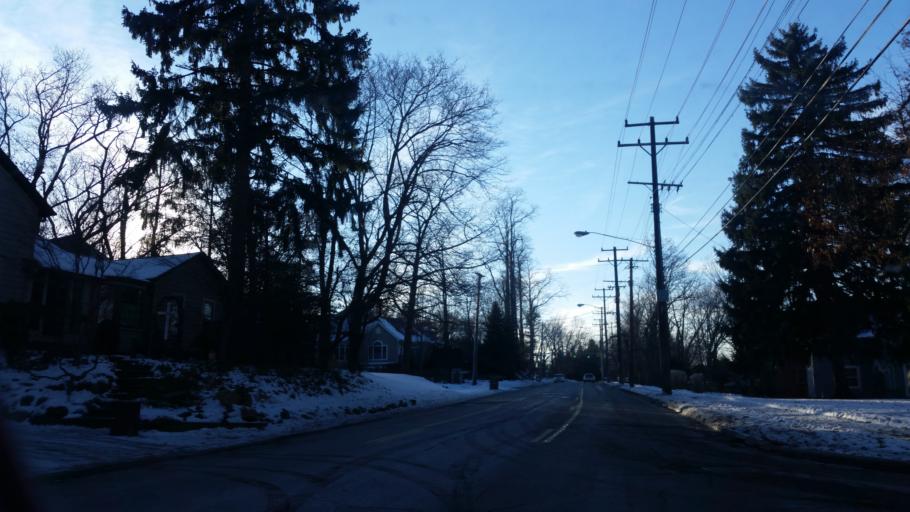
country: US
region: Ohio
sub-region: Cuyahoga County
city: Rocky River
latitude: 41.4717
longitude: -81.8659
